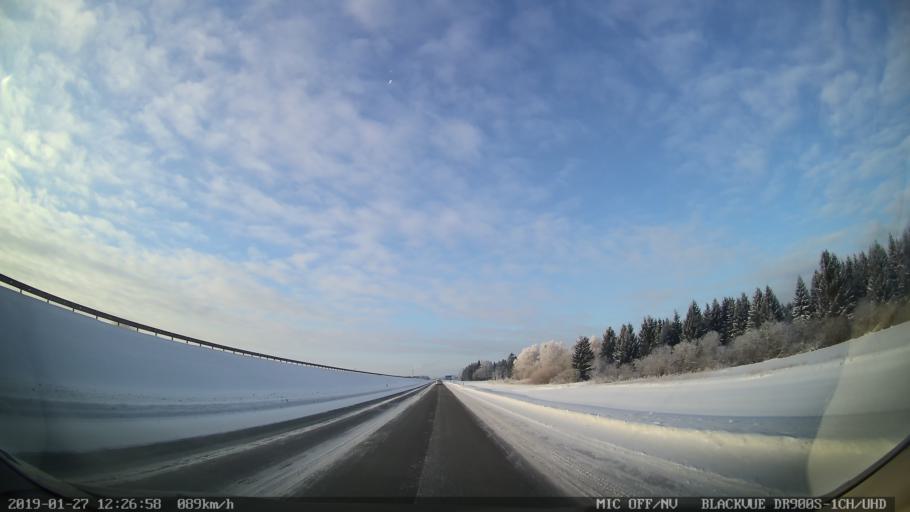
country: EE
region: Harju
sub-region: Maardu linn
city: Maardu
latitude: 59.4514
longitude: 25.0547
